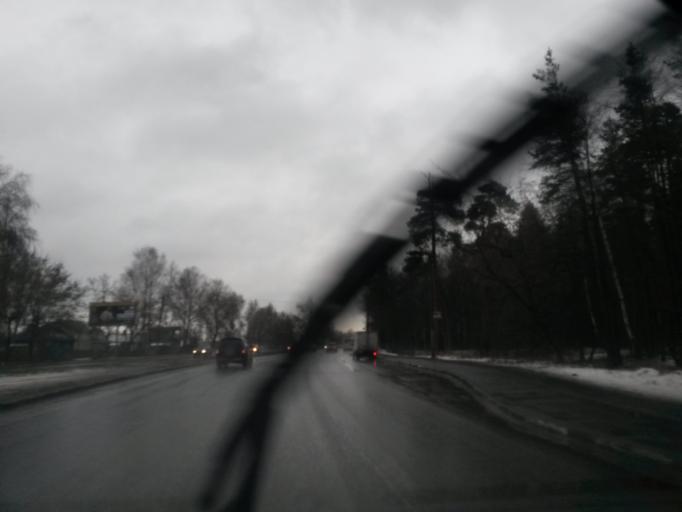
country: RU
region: Jaroslavl
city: Yaroslavl
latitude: 57.6452
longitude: 39.9206
